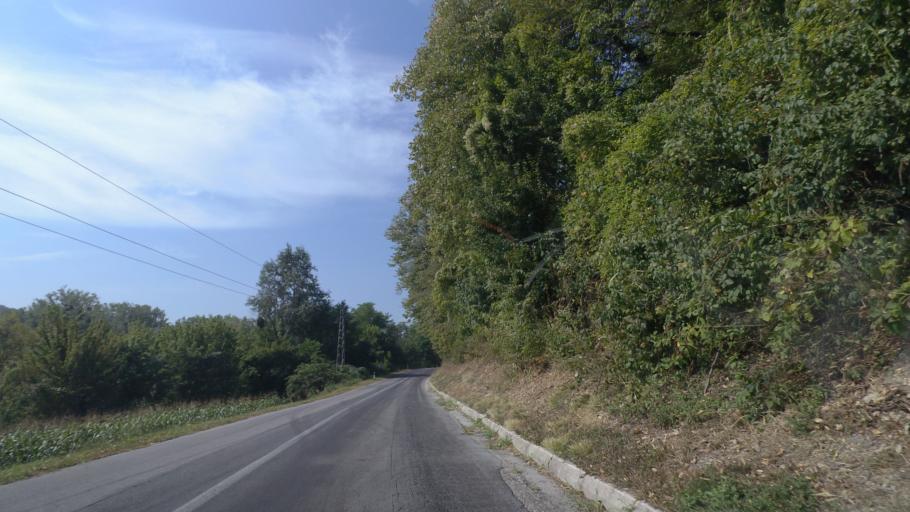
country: BA
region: Republika Srpska
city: Kostajnica
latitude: 45.2164
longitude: 16.5010
